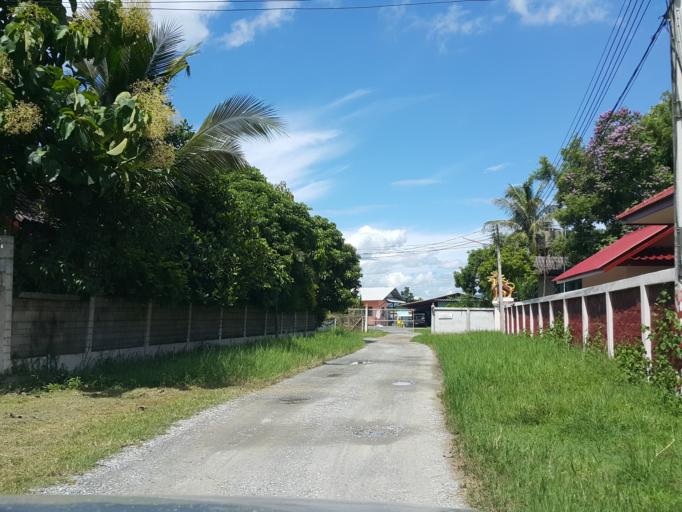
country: TH
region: Chiang Mai
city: San Kamphaeng
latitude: 18.7605
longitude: 99.1270
